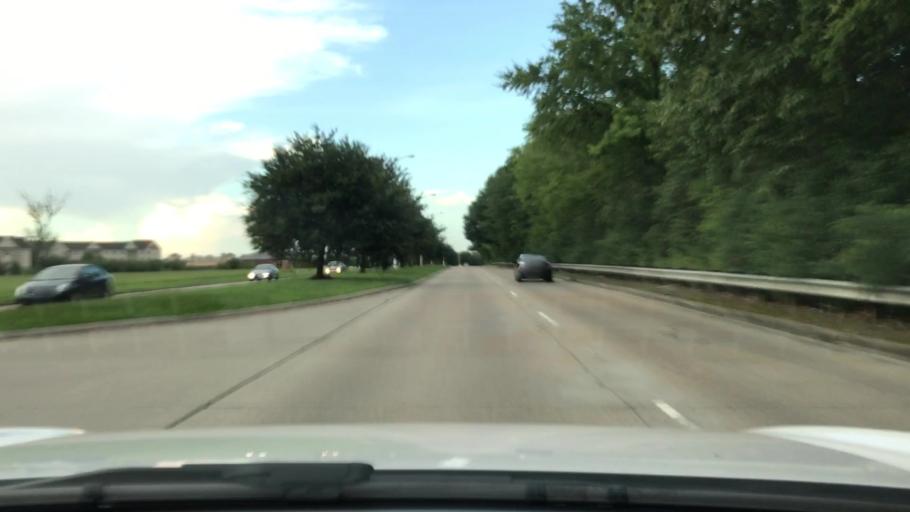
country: US
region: Louisiana
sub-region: East Baton Rouge Parish
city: Westminster
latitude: 30.4277
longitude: -91.1192
